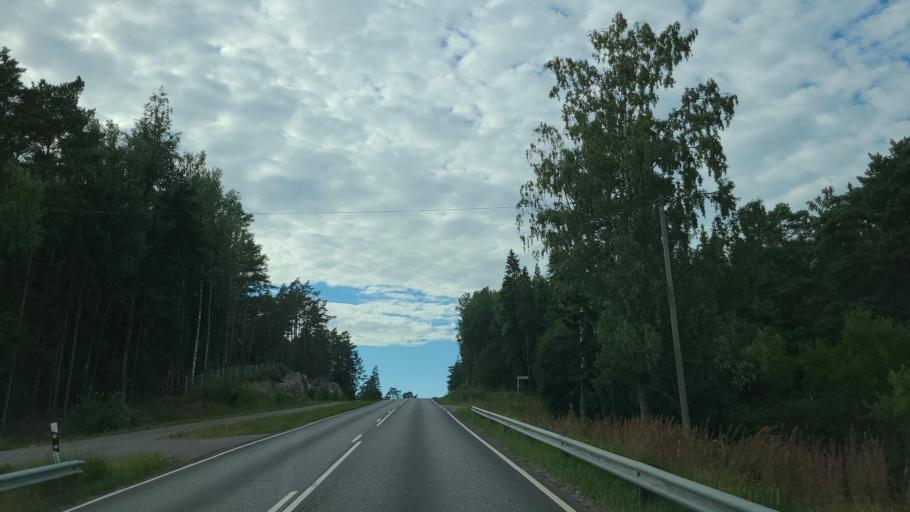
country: FI
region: Varsinais-Suomi
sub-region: Turku
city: Rymaettylae
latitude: 60.3941
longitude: 21.9030
